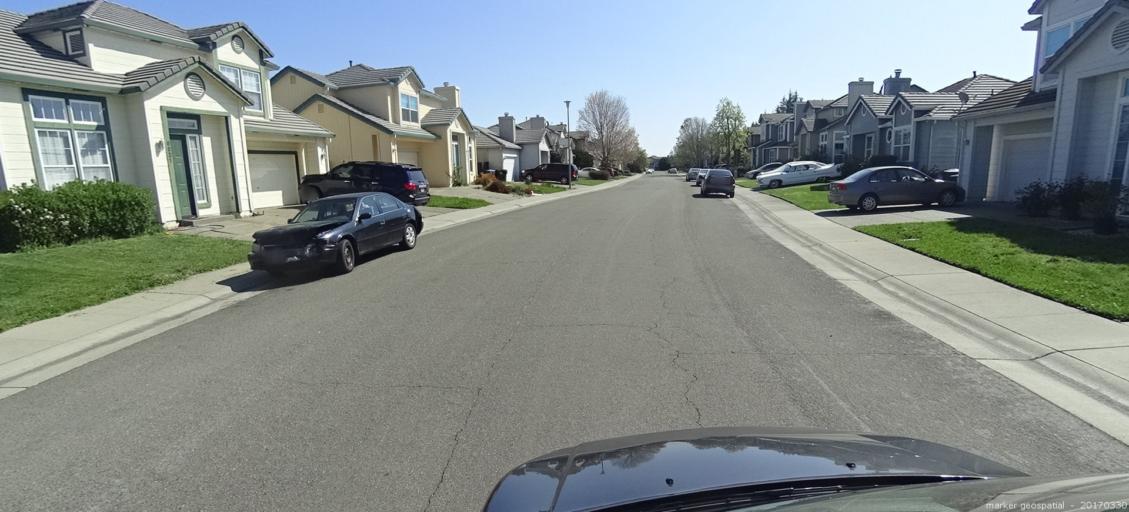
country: US
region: California
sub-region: Sacramento County
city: Laguna
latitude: 38.4400
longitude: -121.4234
